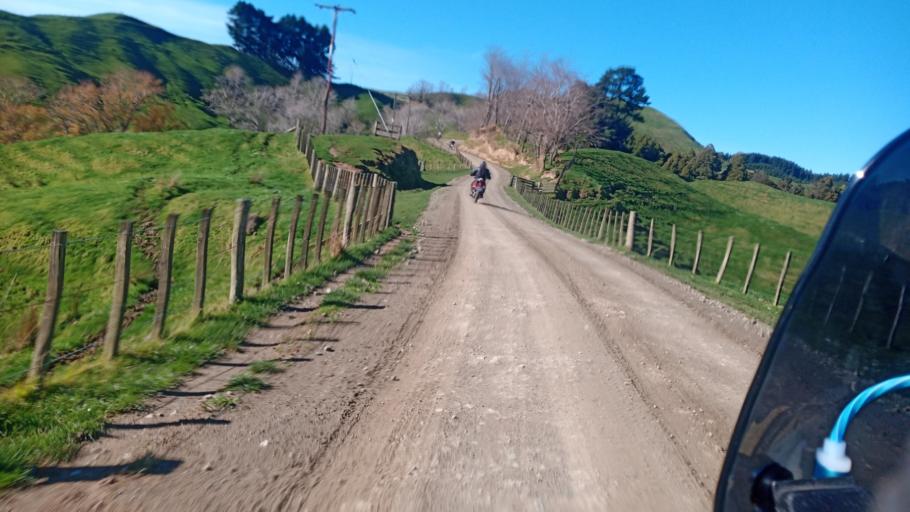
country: NZ
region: Gisborne
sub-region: Gisborne District
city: Gisborne
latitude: -38.2920
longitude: 177.8816
